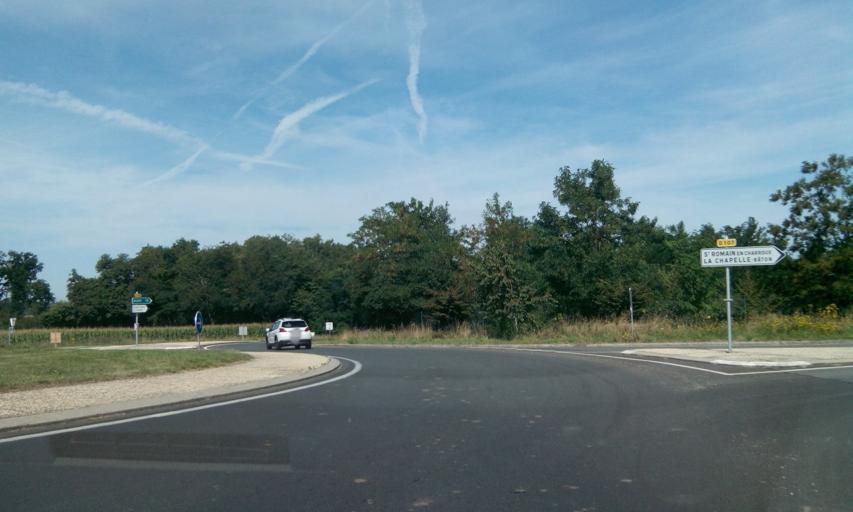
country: FR
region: Poitou-Charentes
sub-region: Departement de la Vienne
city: Charroux
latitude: 46.1529
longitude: 0.3731
